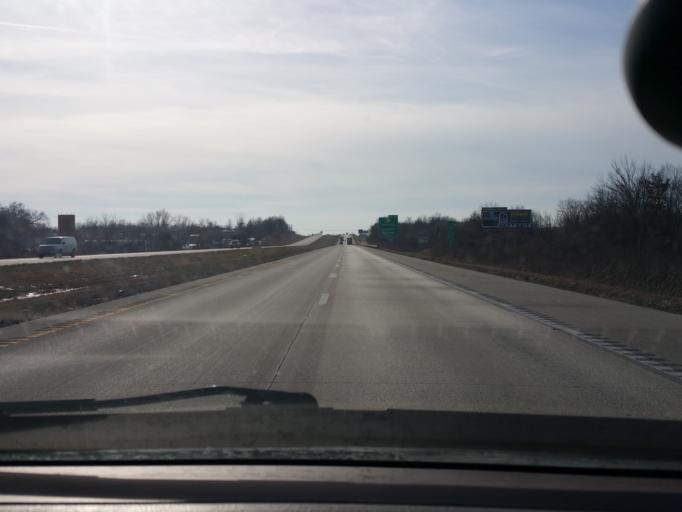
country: US
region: Missouri
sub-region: Clay County
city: Kearney
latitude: 39.3875
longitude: -94.3619
